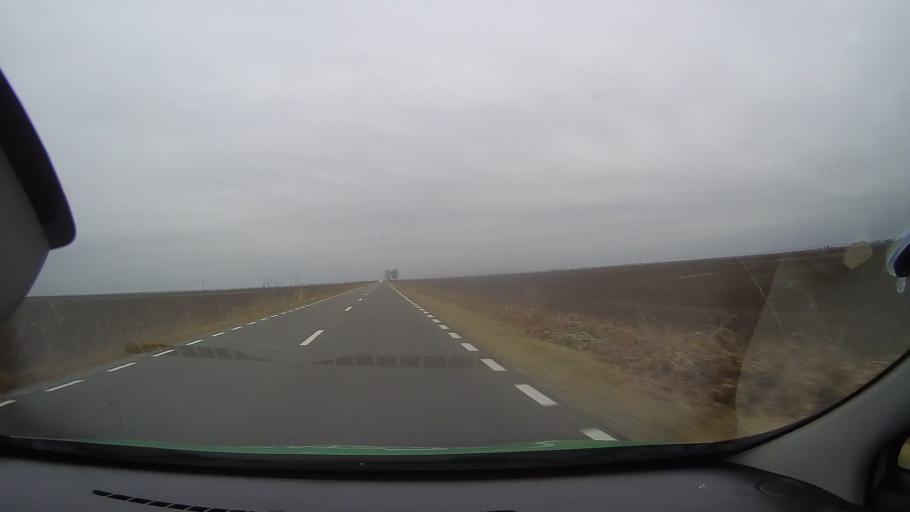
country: RO
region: Ialomita
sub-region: Comuna Gheorghe Lazar
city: Gheorghe Lazar
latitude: 44.6632
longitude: 27.4143
